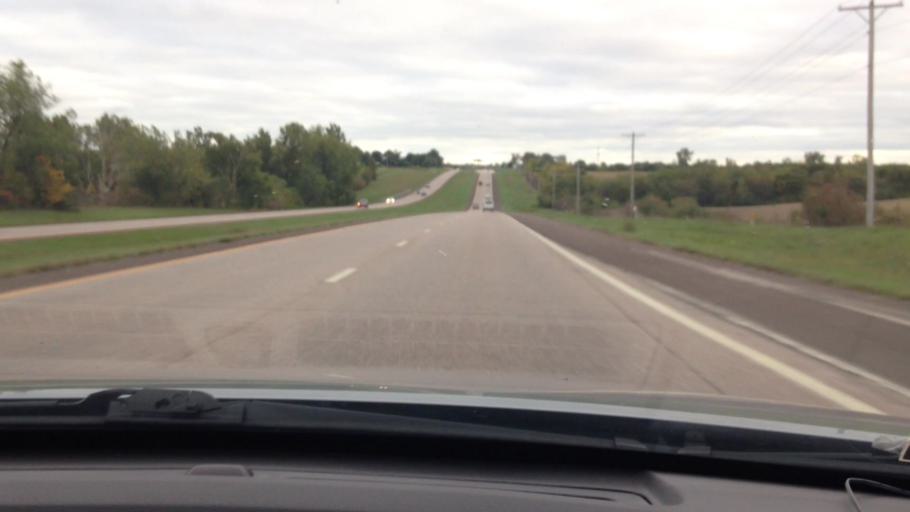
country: US
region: Kansas
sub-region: Leavenworth County
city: Basehor
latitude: 39.1671
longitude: -94.9007
